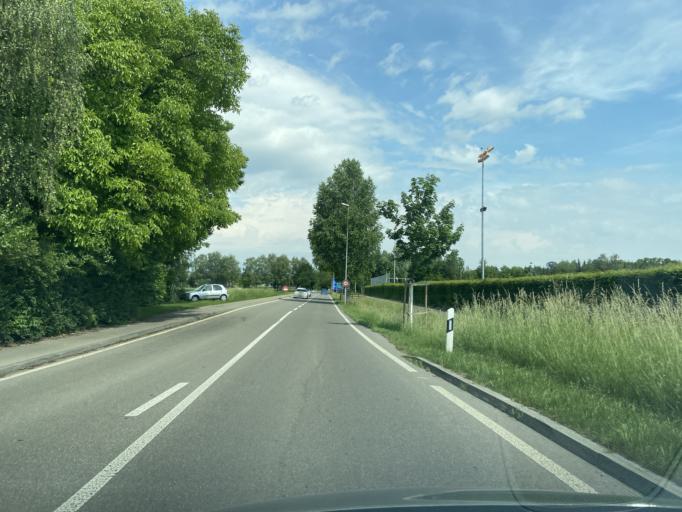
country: CH
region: Zurich
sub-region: Bezirk Uster
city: Duebendorf / Kunklerstrasse
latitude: 47.4076
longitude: 8.6341
